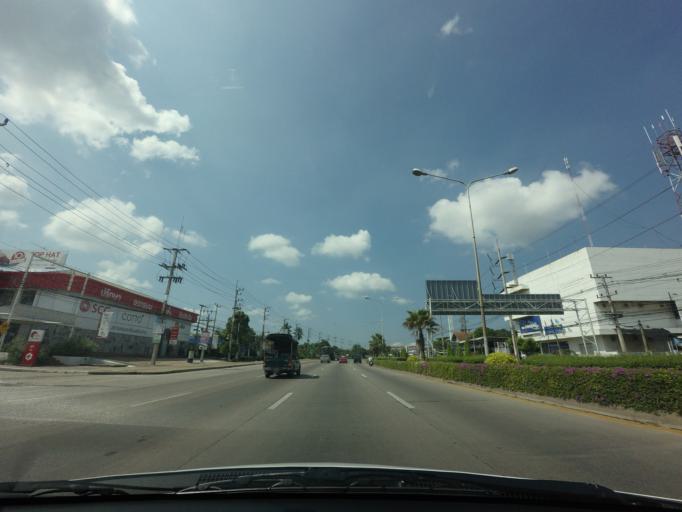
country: TH
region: Nakhon Pathom
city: Sam Phran
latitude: 13.7436
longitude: 100.2133
